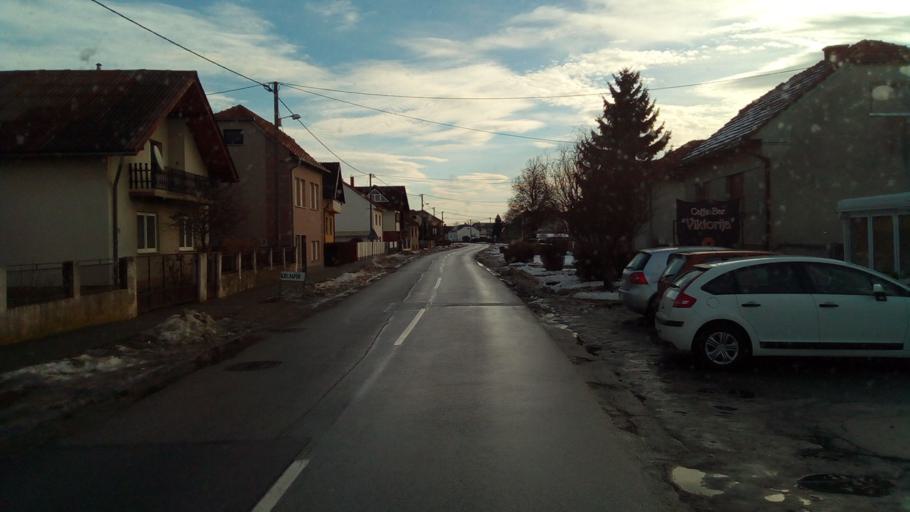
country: HR
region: Medimurska
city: Pribislavec
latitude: 46.3939
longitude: 16.4796
